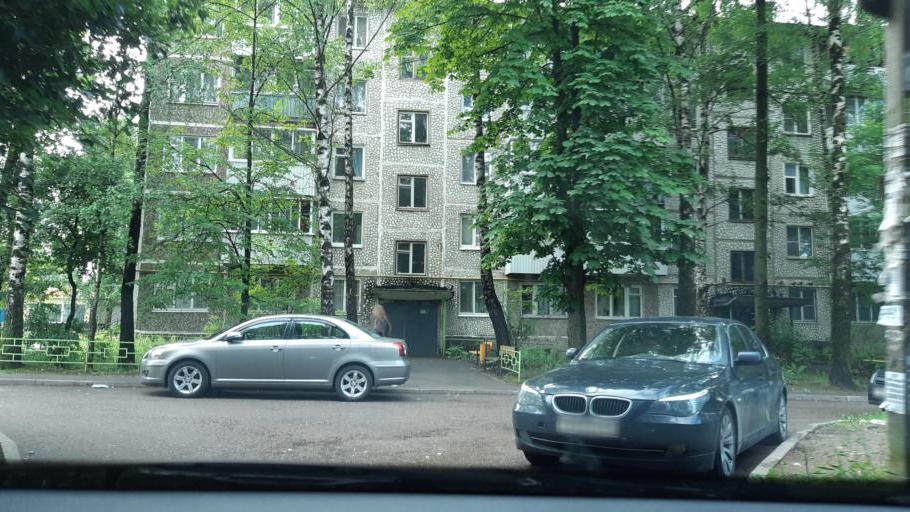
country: RU
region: Smolensk
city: Smolensk
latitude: 54.7655
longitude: 32.0903
